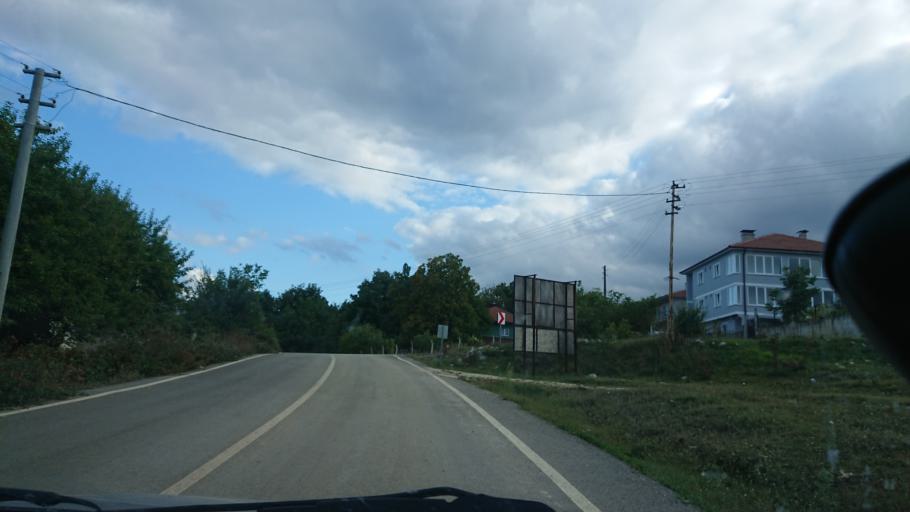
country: TR
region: Bilecik
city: Pazaryeri
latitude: 40.0111
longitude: 29.7983
